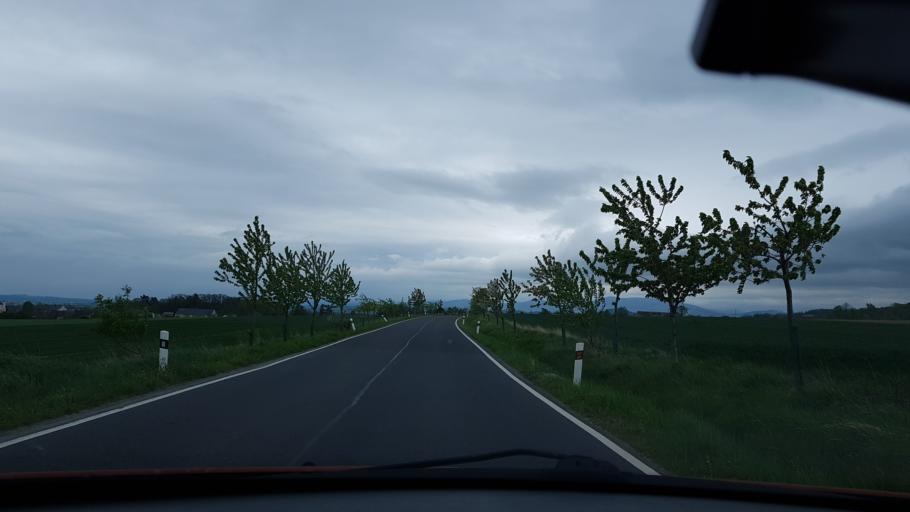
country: CZ
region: Olomoucky
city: Javornik
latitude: 50.4123
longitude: 16.9829
